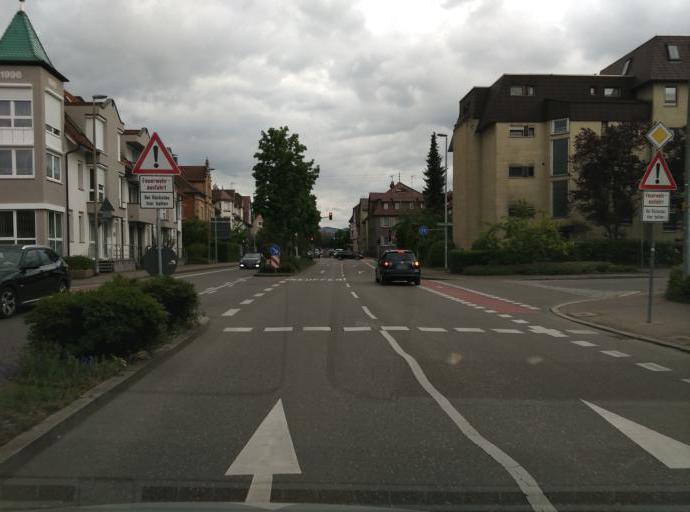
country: DE
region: Baden-Wuerttemberg
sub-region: Regierungsbezirk Stuttgart
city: Nurtingen
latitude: 48.6237
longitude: 9.3429
